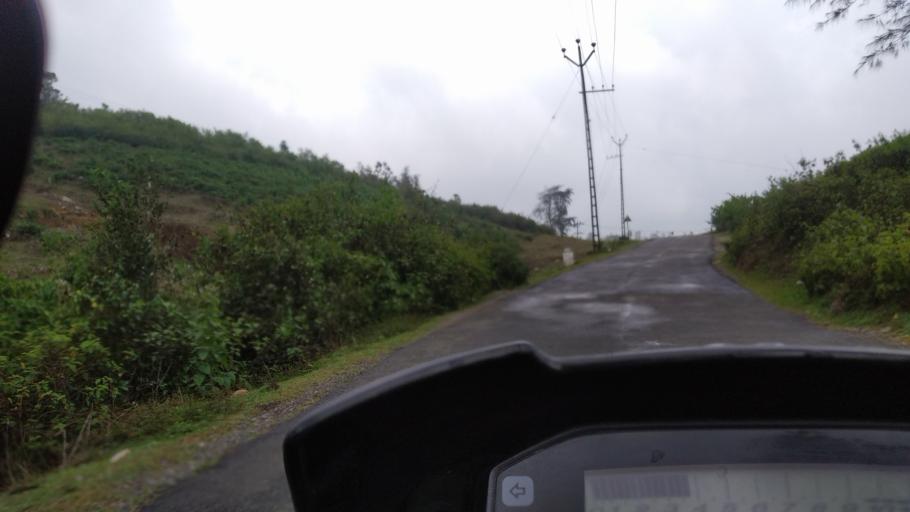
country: IN
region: Kerala
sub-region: Kottayam
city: Erattupetta
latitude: 9.6339
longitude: 76.9488
